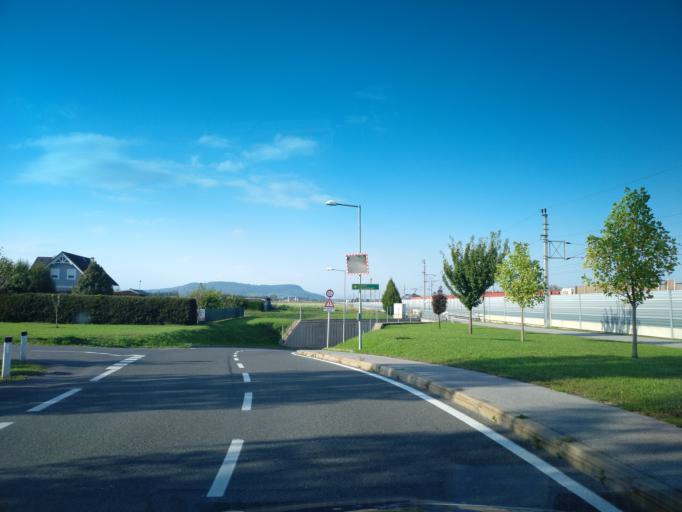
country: AT
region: Styria
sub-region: Politischer Bezirk Leibnitz
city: Kaindorf an der Sulm
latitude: 46.8035
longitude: 15.5418
